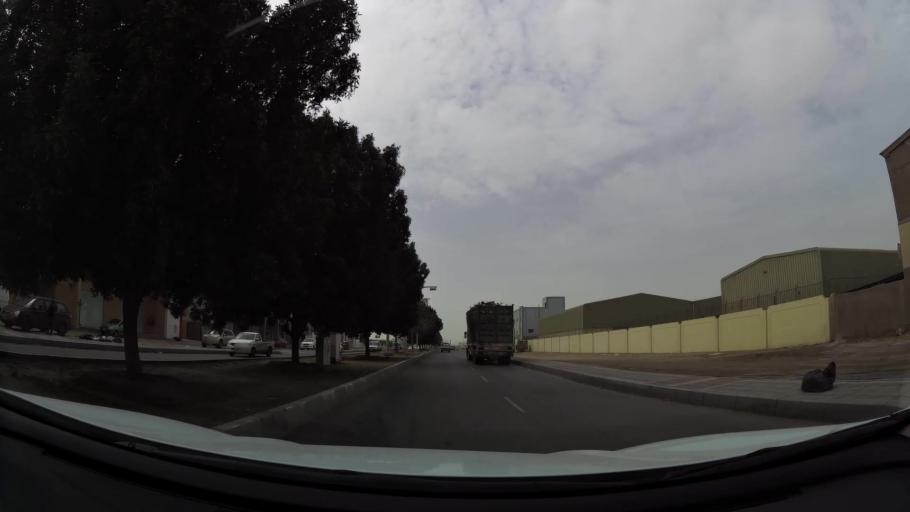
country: AE
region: Abu Dhabi
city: Abu Dhabi
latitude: 24.3543
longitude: 54.4877
